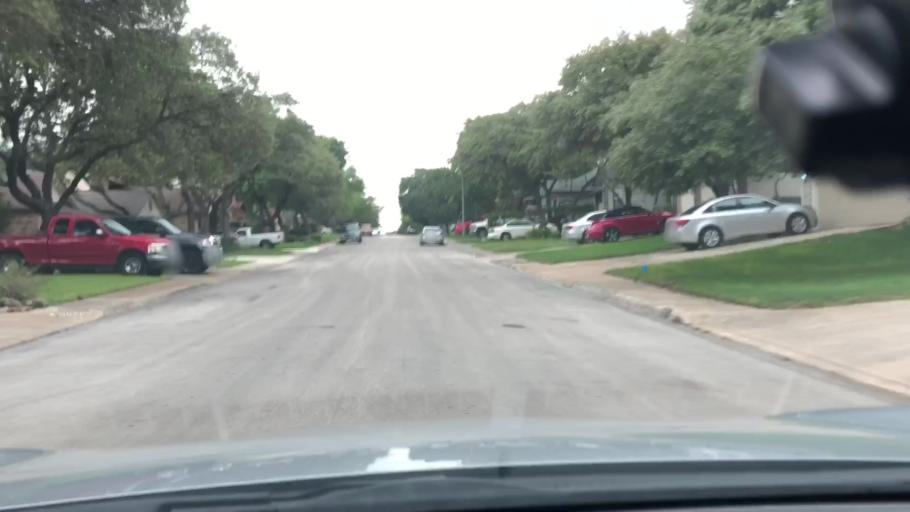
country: US
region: Texas
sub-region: Bexar County
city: Leon Valley
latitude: 29.5059
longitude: -98.6714
